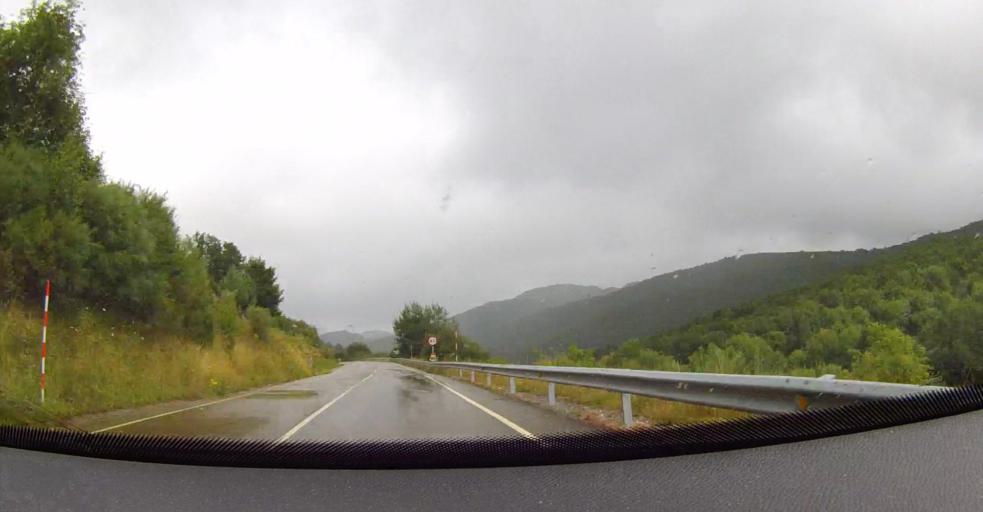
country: ES
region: Castille and Leon
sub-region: Provincia de Leon
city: Marana
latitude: 43.0703
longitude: -5.1888
